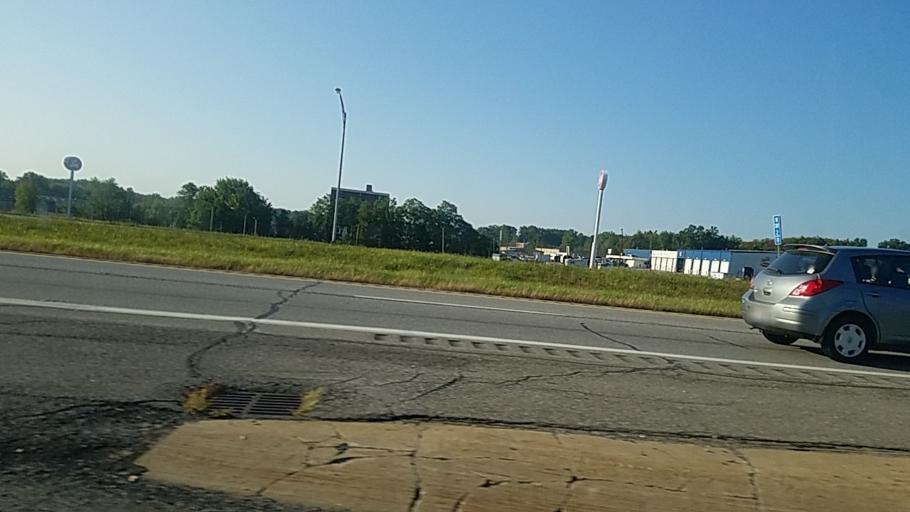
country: US
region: Ohio
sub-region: Trumbull County
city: Girard
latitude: 41.1228
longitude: -80.7124
